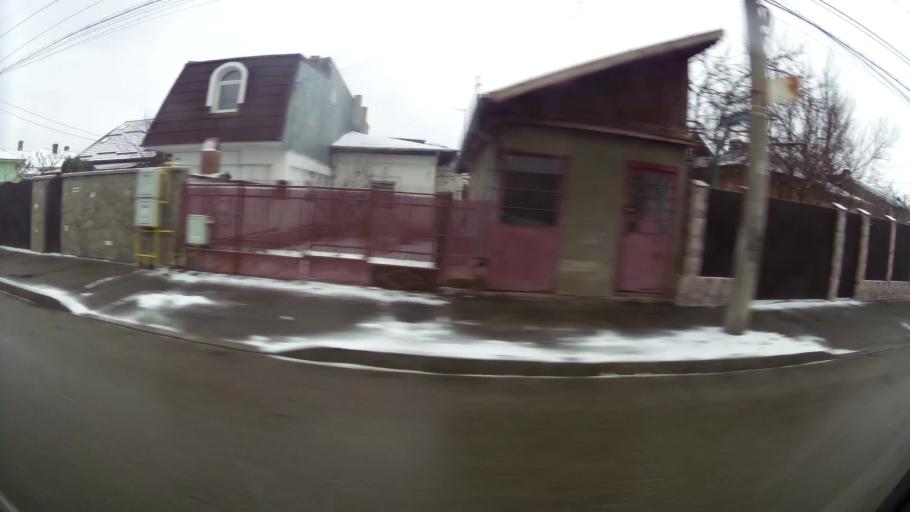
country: RO
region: Prahova
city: Ploiesti
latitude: 44.9308
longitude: 26.0435
